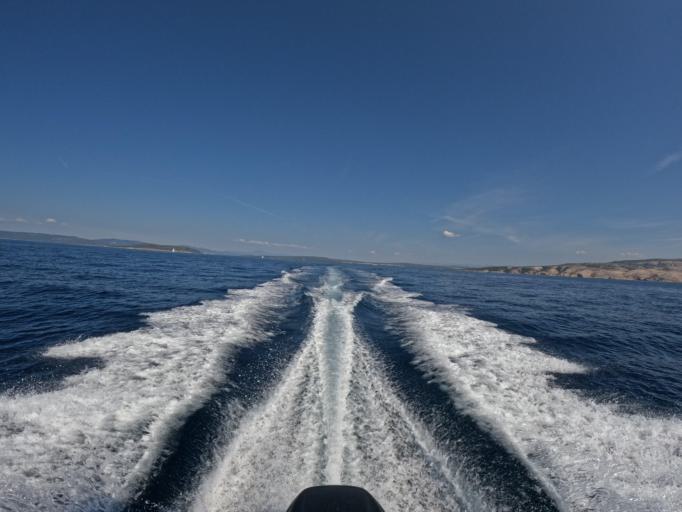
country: HR
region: Primorsko-Goranska
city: Punat
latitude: 44.9298
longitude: 14.6180
